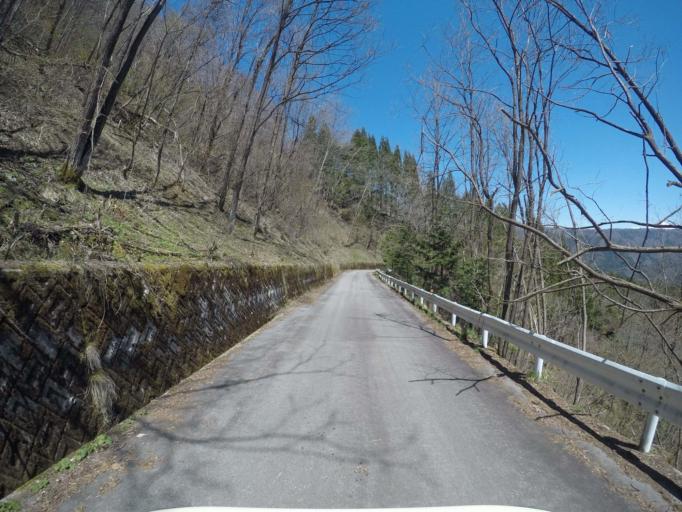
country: JP
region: Gifu
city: Takayama
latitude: 36.1559
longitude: 137.4293
